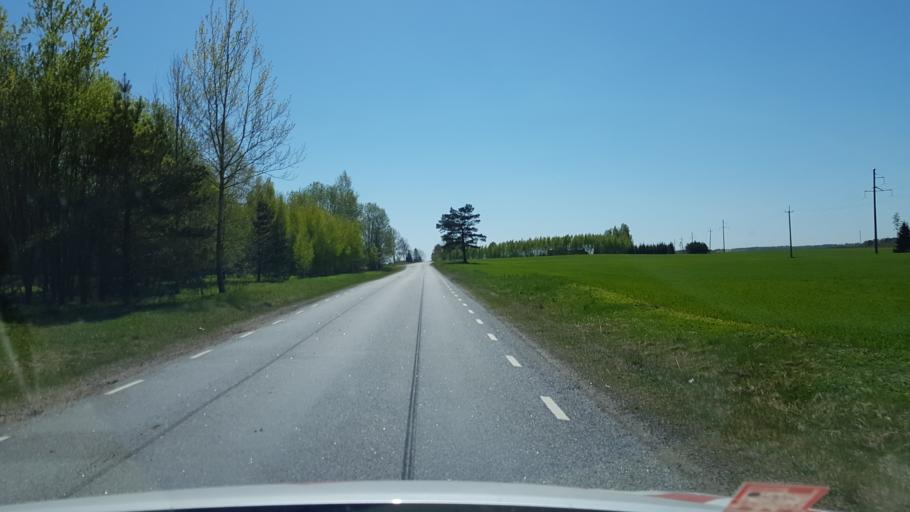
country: EE
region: Vorumaa
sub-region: Voru linn
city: Voru
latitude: 57.9319
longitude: 26.9518
